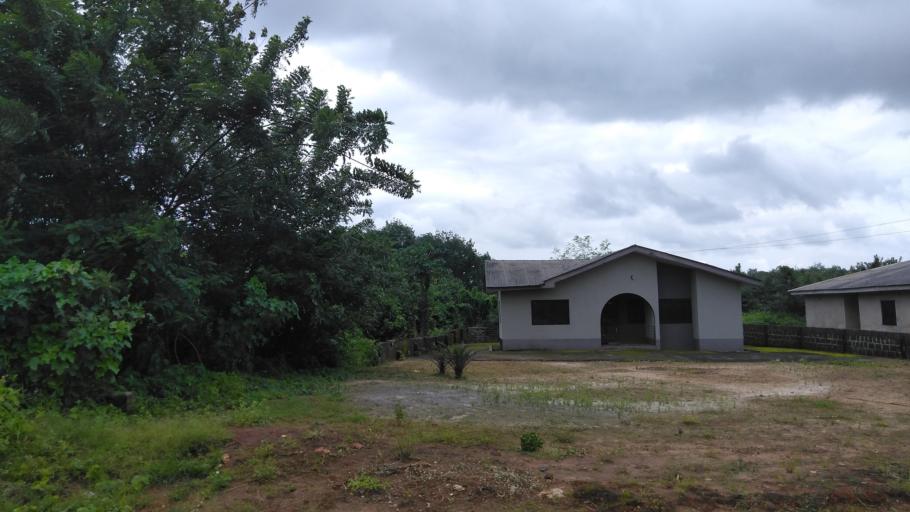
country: NG
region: Ogun
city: Abigi
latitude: 6.5982
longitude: 4.4879
